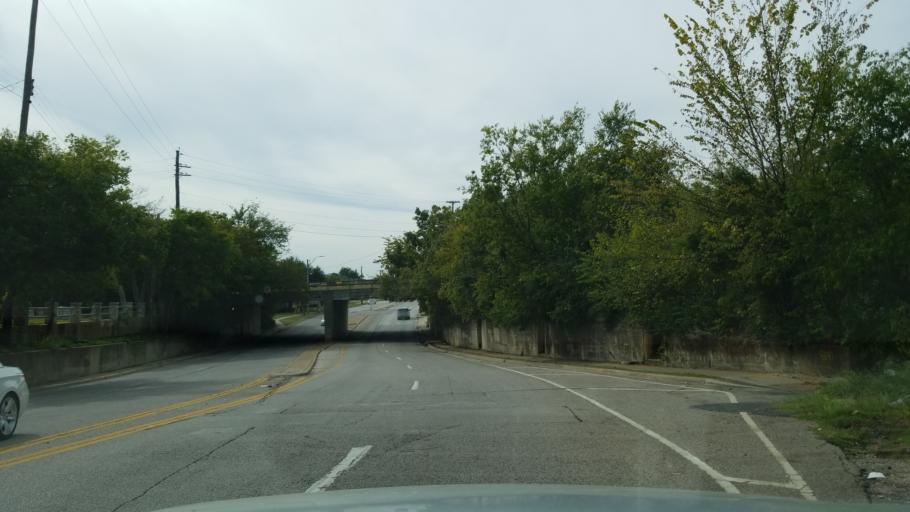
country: US
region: Texas
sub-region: Dallas County
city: Dallas
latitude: 32.7791
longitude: -96.7378
